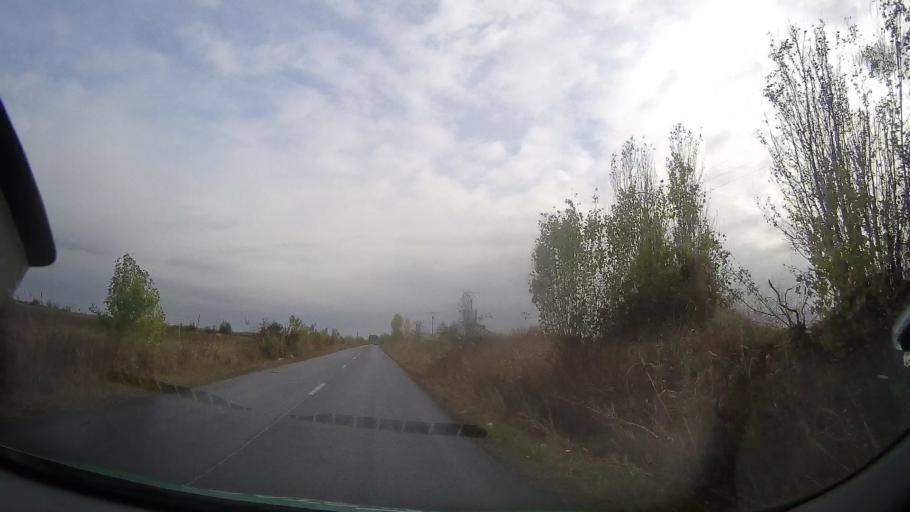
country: RO
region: Ialomita
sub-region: Comuna Maia
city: Maia
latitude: 44.7503
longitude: 26.3909
